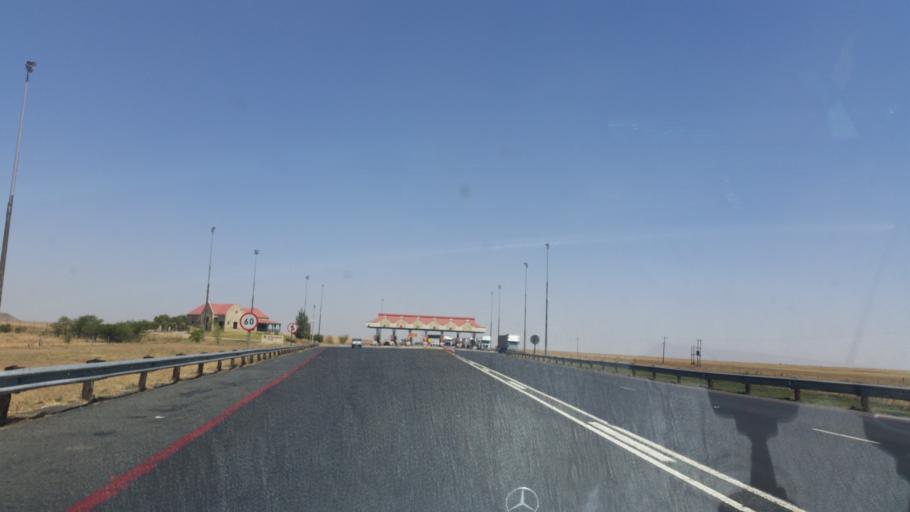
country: ZA
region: Orange Free State
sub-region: Lejweleputswa District Municipality
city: Brandfort
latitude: -28.7973
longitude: 26.6924
